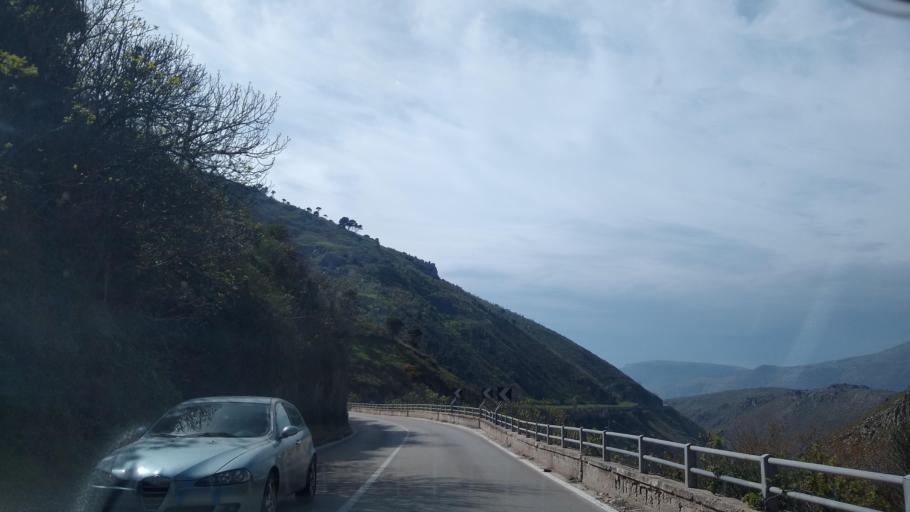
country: IT
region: Sicily
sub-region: Palermo
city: Montelepre
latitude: 38.0509
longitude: 13.1877
